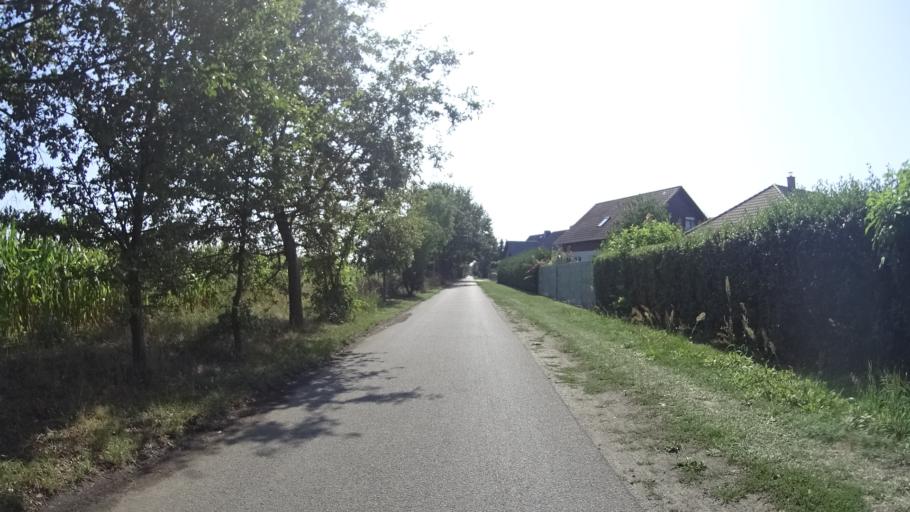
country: DE
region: Brandenburg
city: Werben
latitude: 51.8120
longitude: 14.1972
